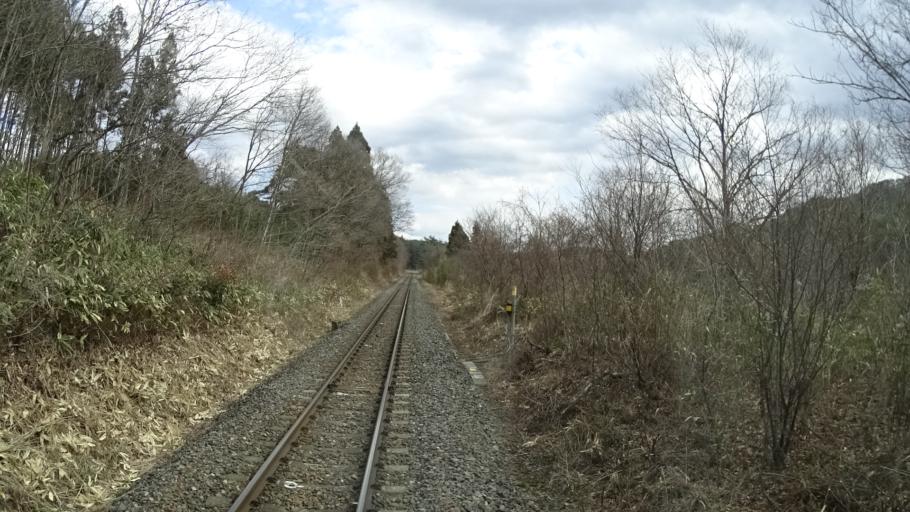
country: JP
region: Iwate
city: Tono
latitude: 39.3338
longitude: 141.3591
